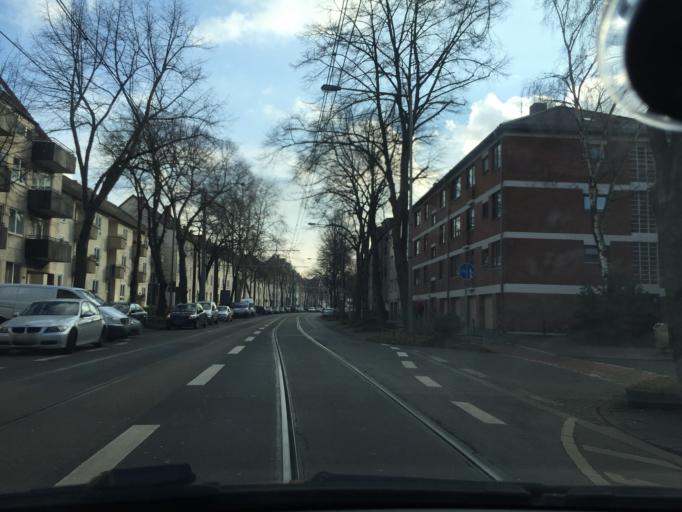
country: DE
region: North Rhine-Westphalia
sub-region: Regierungsbezirk Koln
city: Poll
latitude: 50.9197
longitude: 6.9864
